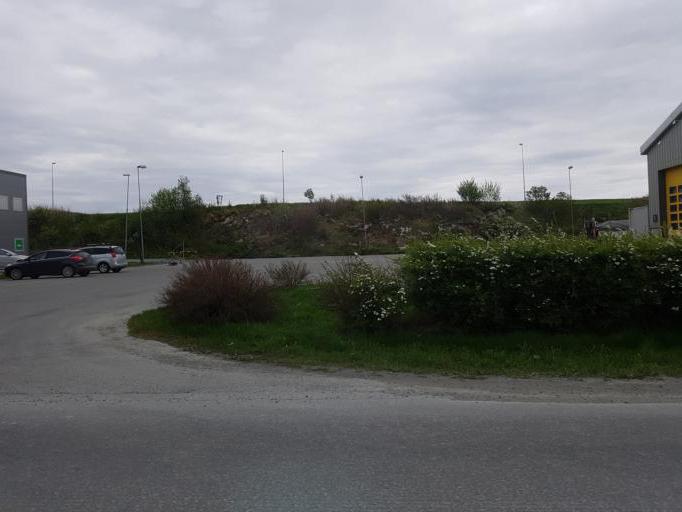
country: NO
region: Nord-Trondelag
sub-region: Levanger
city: Levanger
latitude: 63.7376
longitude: 11.2813
